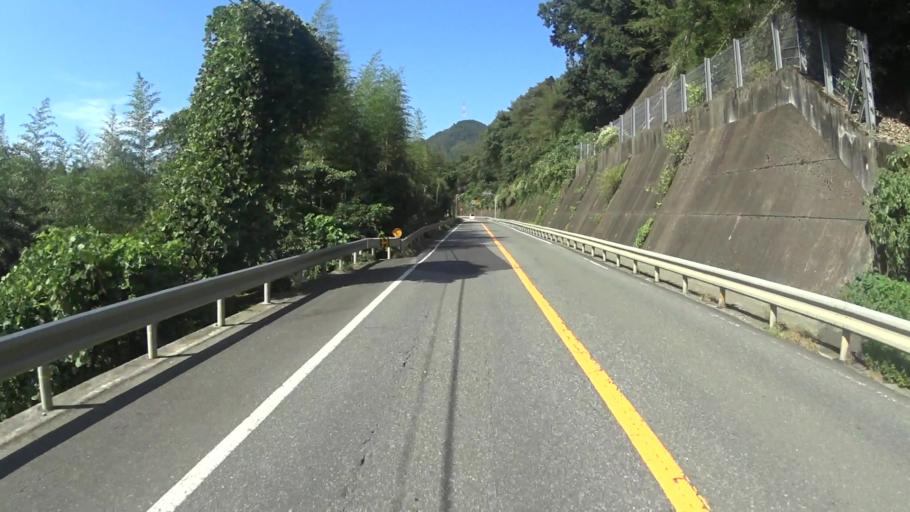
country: JP
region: Kyoto
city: Ayabe
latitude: 35.2983
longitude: 135.3221
